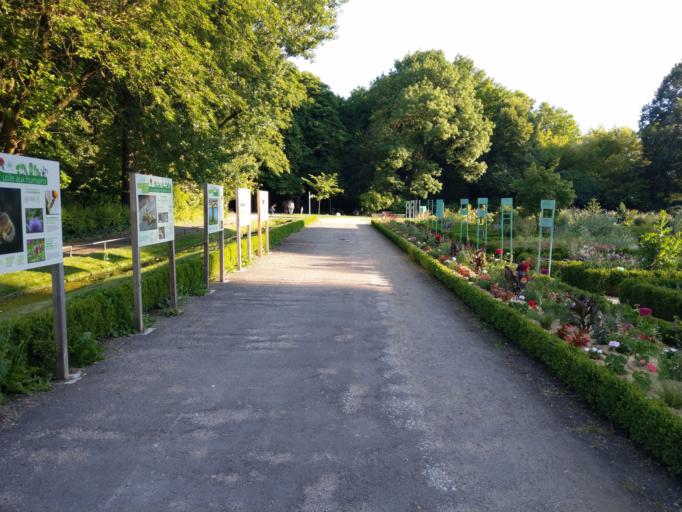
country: FR
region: Bourgogne
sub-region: Departement de la Cote-d'Or
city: Dijon
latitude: 47.3213
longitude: 5.0283
